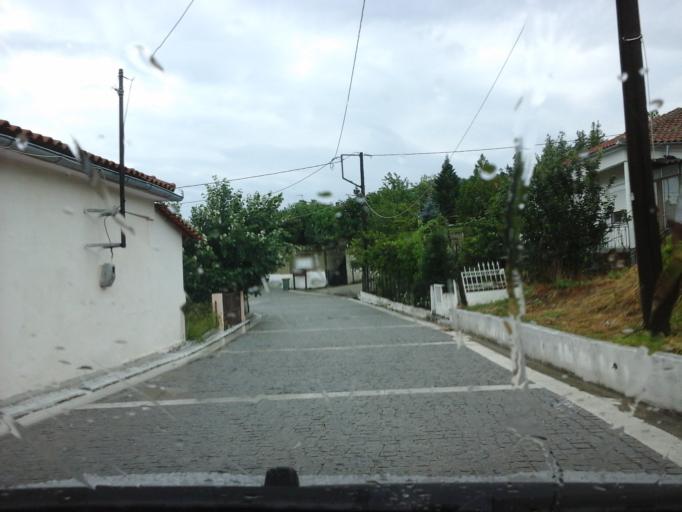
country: GR
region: East Macedonia and Thrace
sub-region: Nomos Evrou
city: Soufli
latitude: 41.1283
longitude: 26.2260
